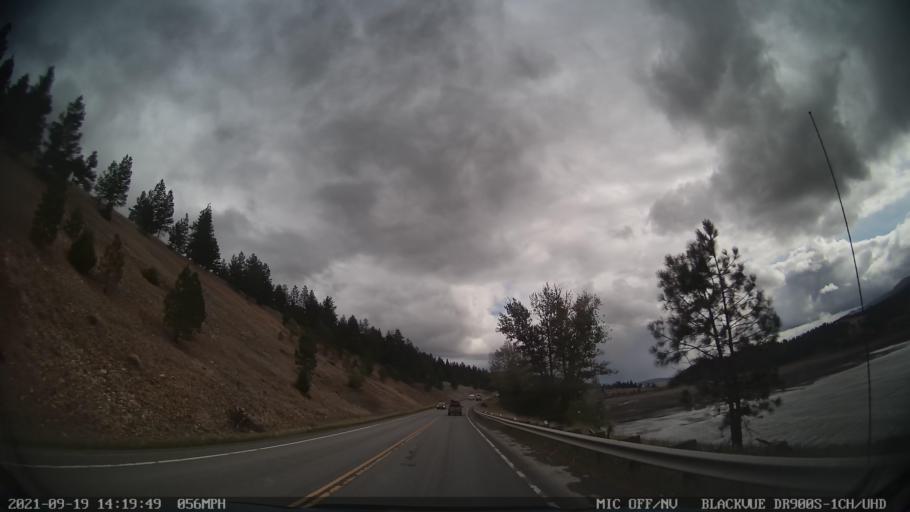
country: US
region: Montana
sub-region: Lewis and Clark County
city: Lincoln
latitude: 46.7963
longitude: -112.7902
